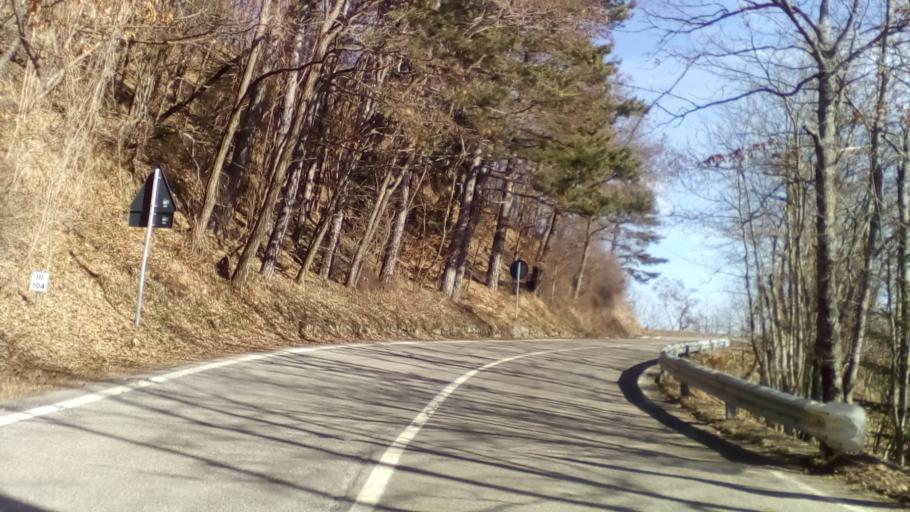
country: IT
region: Emilia-Romagna
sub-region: Provincia di Modena
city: Pievepelago
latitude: 44.2151
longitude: 10.6242
